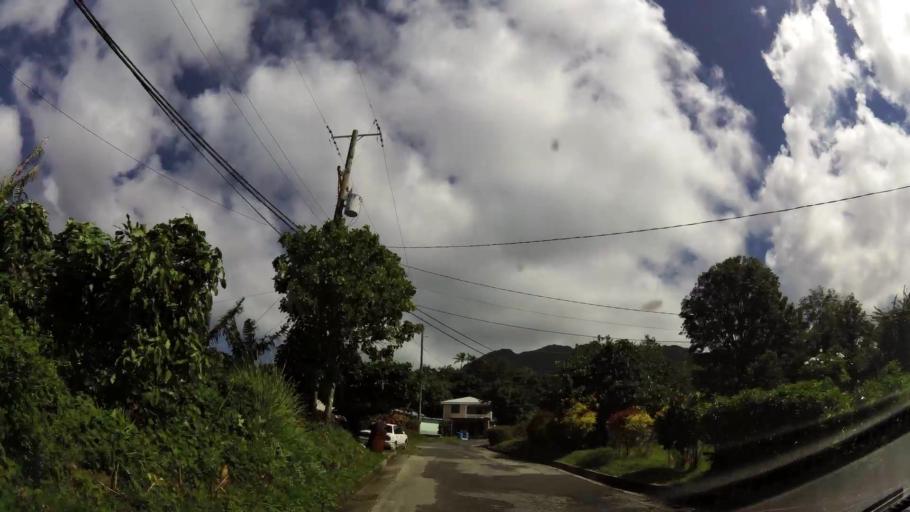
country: DM
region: Saint John
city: Portsmouth
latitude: 15.6052
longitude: -61.4610
